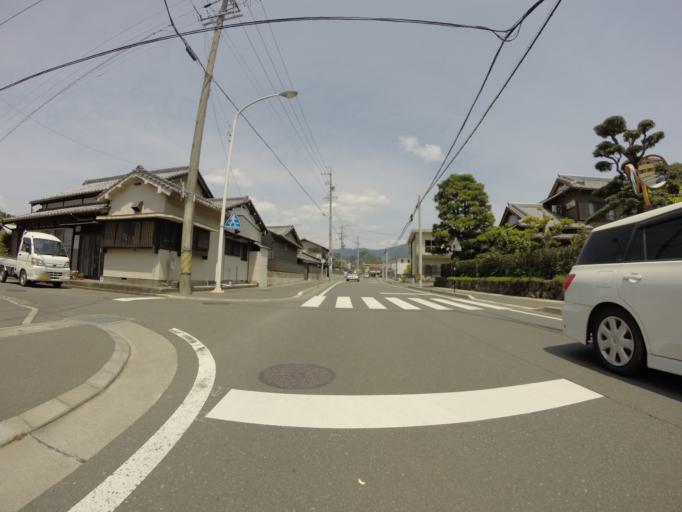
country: JP
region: Shizuoka
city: Shizuoka-shi
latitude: 35.0196
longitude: 138.4229
